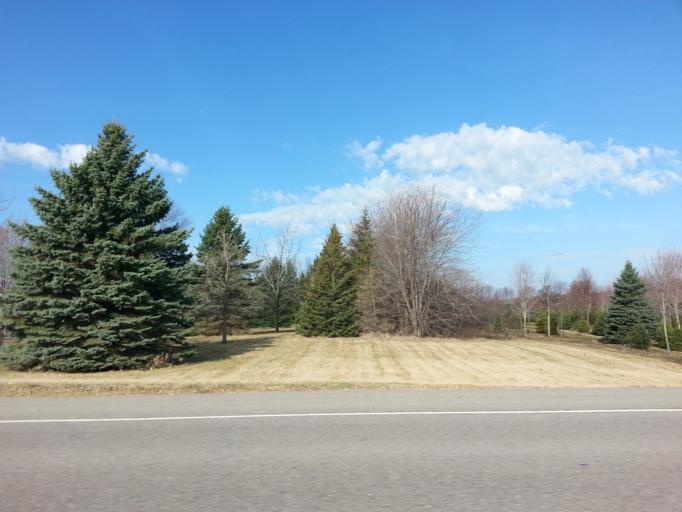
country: US
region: Minnesota
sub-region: Washington County
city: Cottage Grove
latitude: 44.8535
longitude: -92.9033
